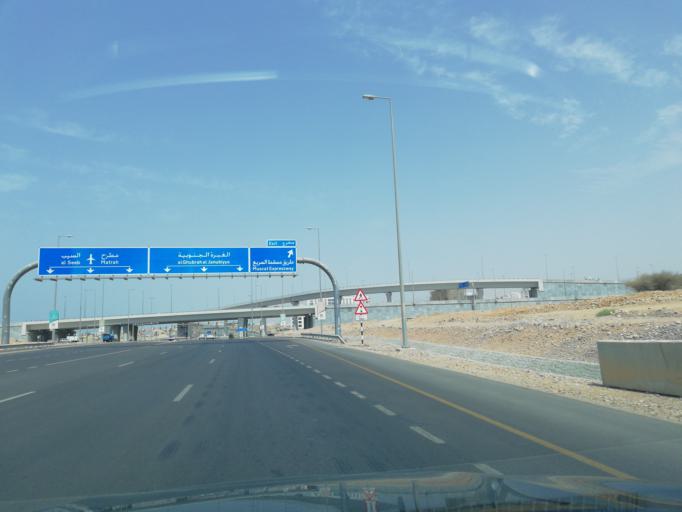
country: OM
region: Muhafazat Masqat
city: Bawshar
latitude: 23.5825
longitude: 58.3299
